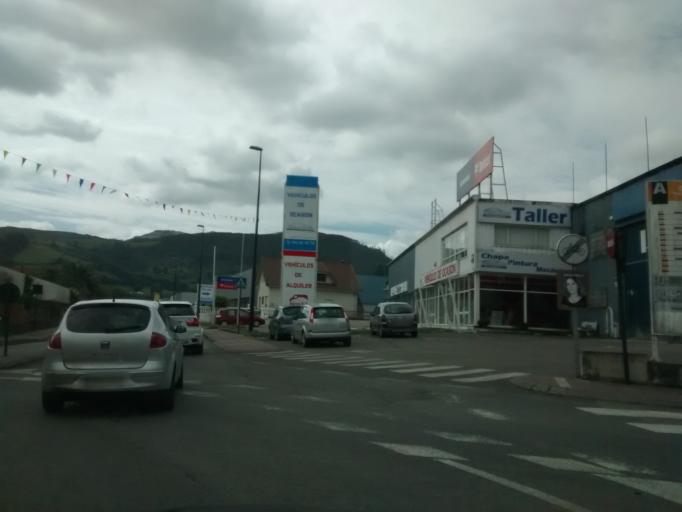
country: ES
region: Cantabria
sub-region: Provincia de Cantabria
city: Cartes
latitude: 43.3239
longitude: -4.0717
